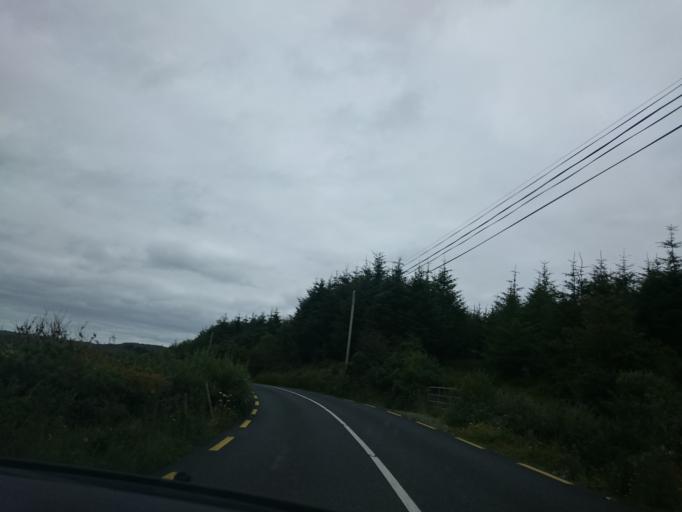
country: IE
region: Connaught
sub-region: County Galway
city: Clifden
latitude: 53.5163
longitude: -10.0408
